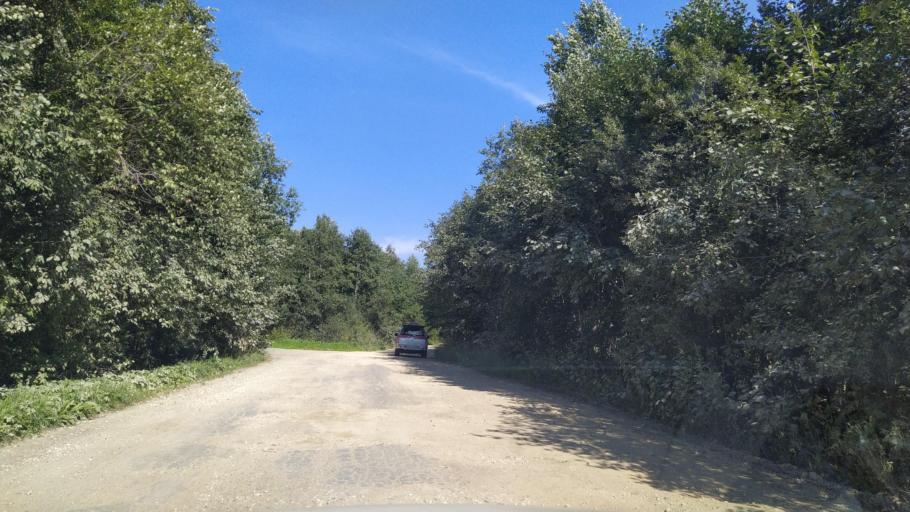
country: RU
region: Leningrad
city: Siverskiy
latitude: 59.2903
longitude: 30.0313
